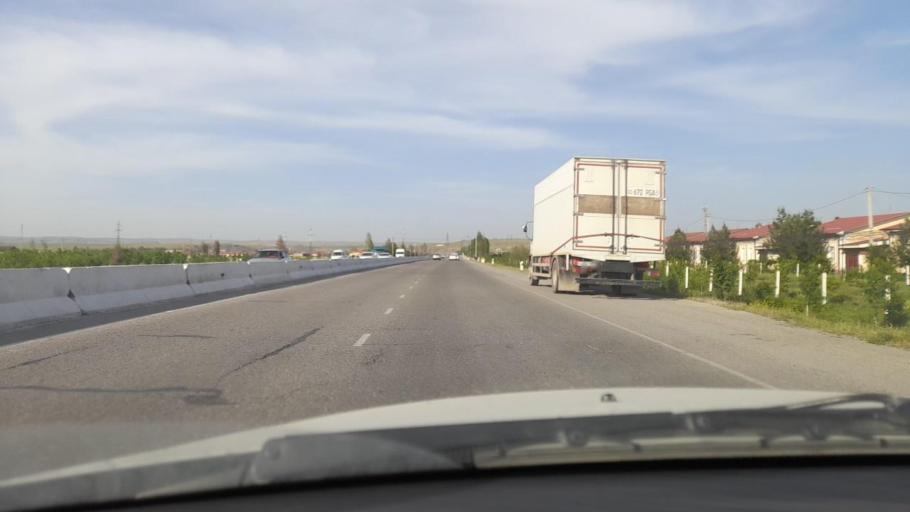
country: UZ
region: Jizzax
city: Jizzax
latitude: 40.0168
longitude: 67.6079
